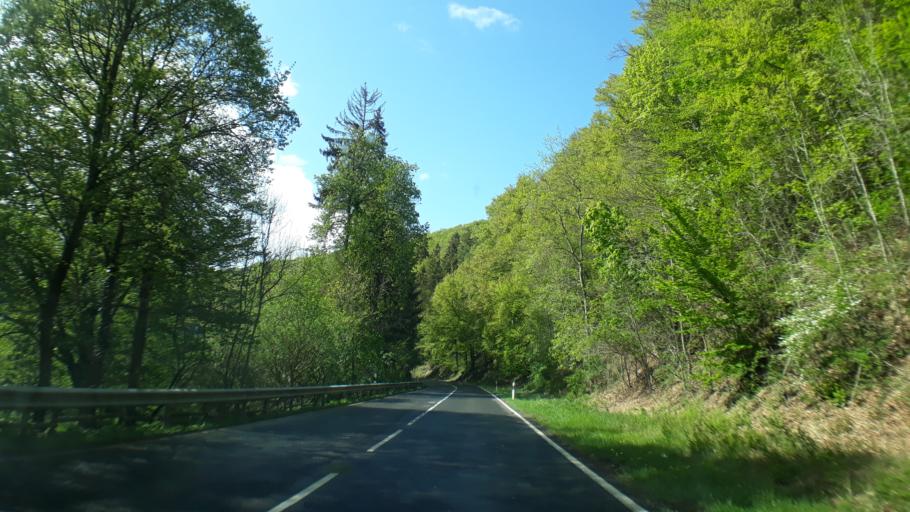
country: DE
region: North Rhine-Westphalia
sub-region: Regierungsbezirk Koln
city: Kall
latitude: 50.5139
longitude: 6.5803
